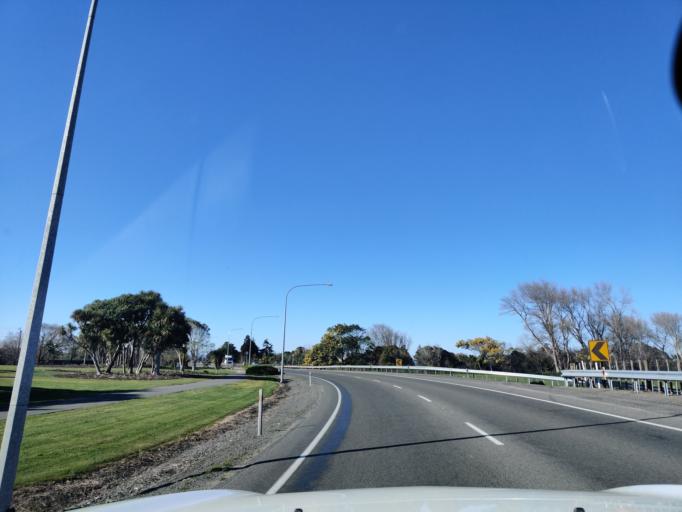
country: NZ
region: Manawatu-Wanganui
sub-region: Palmerston North City
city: Palmerston North
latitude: -40.2373
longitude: 175.5759
